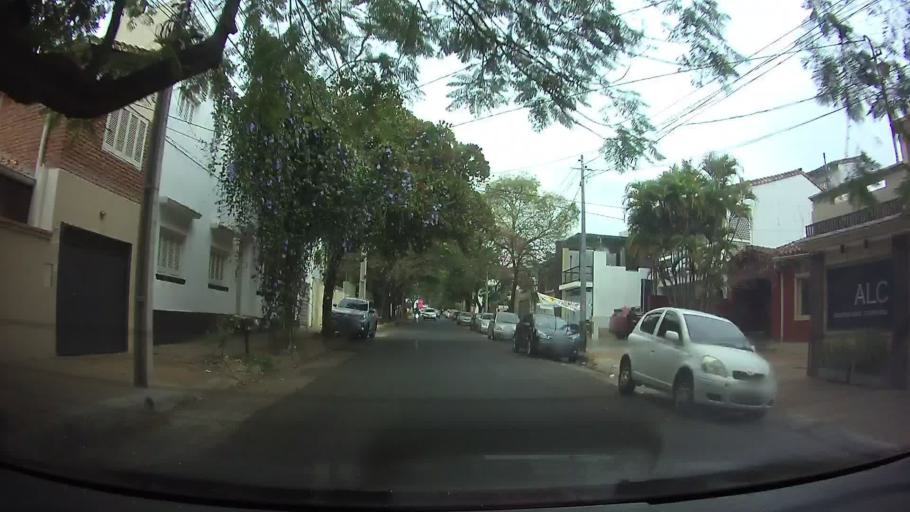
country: PY
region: Asuncion
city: Asuncion
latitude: -25.2855
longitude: -57.6140
